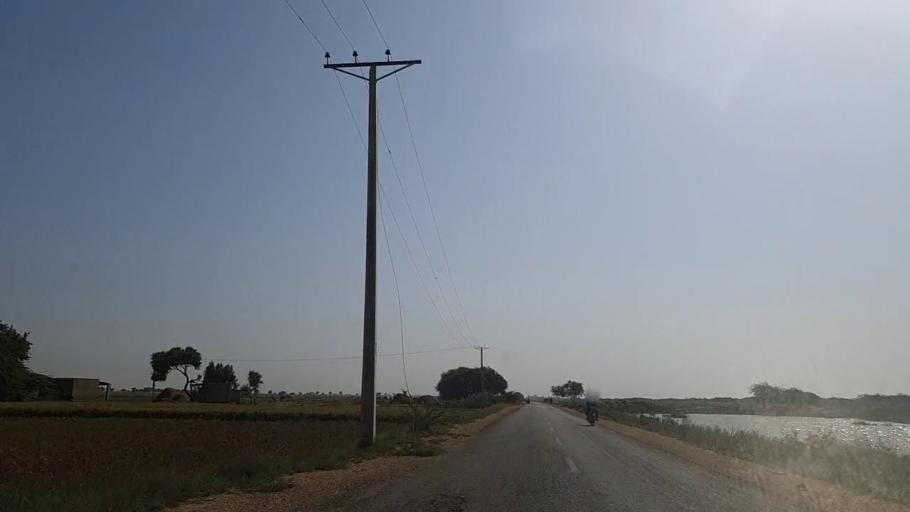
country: PK
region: Sindh
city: Jati
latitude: 24.5401
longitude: 68.2797
